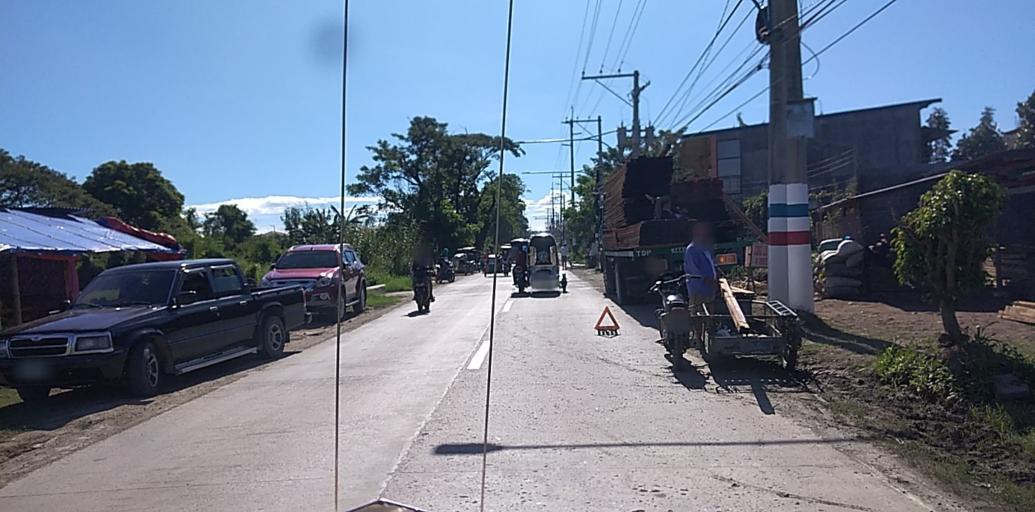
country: PH
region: Central Luzon
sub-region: Province of Pampanga
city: San Luis
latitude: 15.0466
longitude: 120.7861
